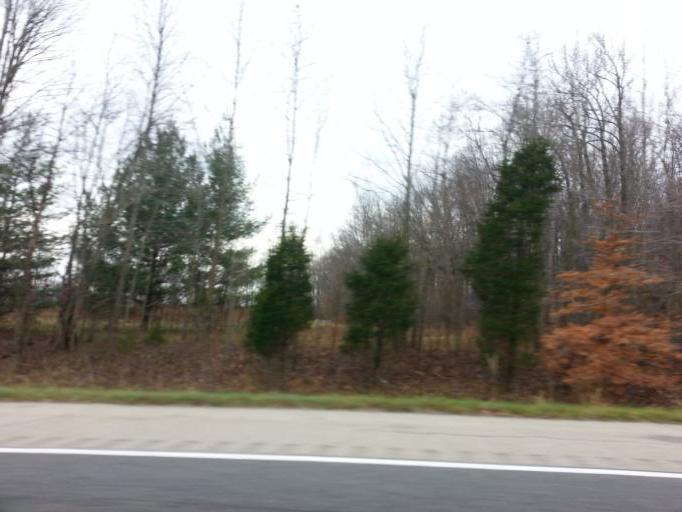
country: US
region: Indiana
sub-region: Ripley County
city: Batesville
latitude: 39.2840
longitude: -85.1537
